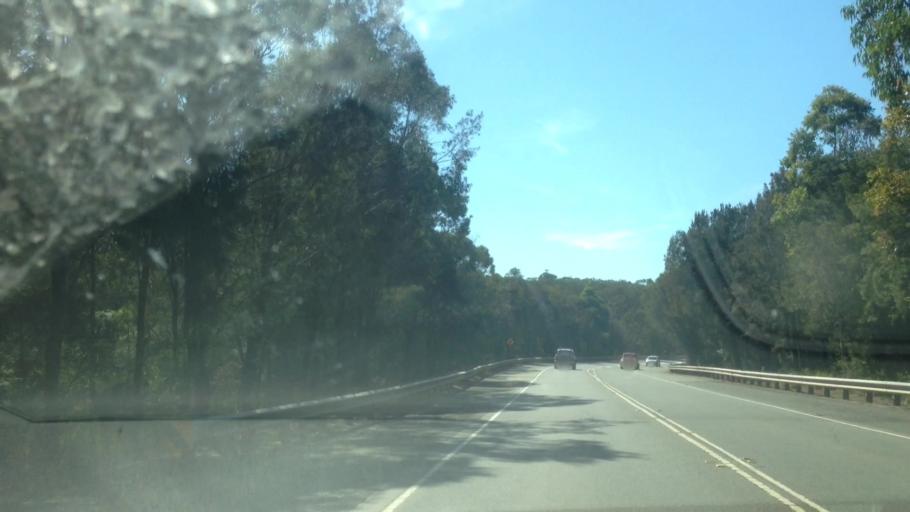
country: AU
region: New South Wales
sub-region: Lake Macquarie Shire
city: Toronto
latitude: -32.9862
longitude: 151.5143
